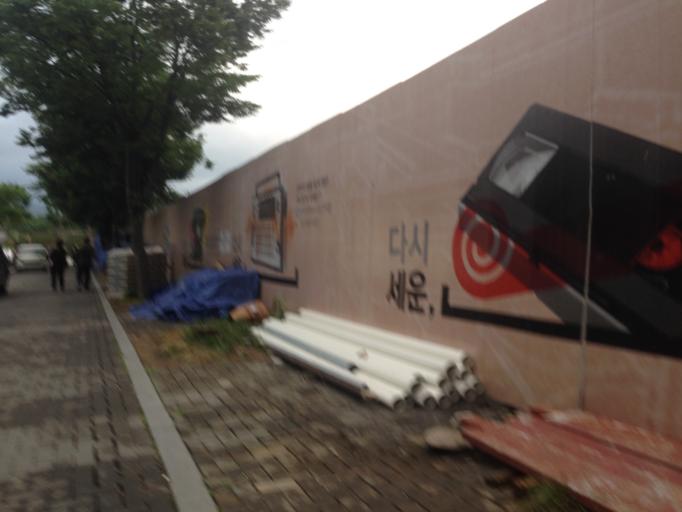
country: KR
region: Seoul
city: Seoul
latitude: 37.5698
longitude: 126.9950
